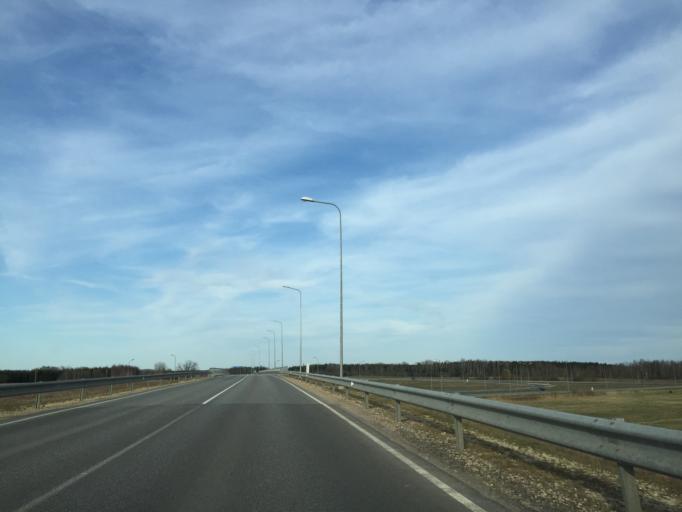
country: LV
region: Lielvarde
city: Lielvarde
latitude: 56.8061
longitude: 24.8793
